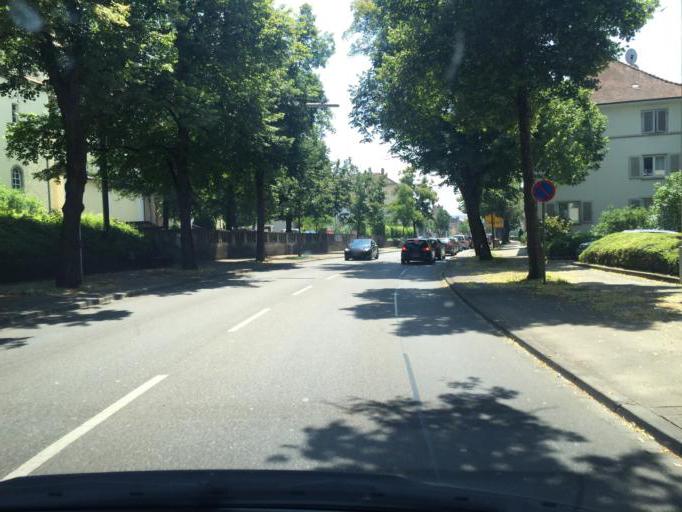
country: DE
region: Baden-Wuerttemberg
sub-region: Freiburg Region
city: Singen
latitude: 47.7529
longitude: 8.8417
